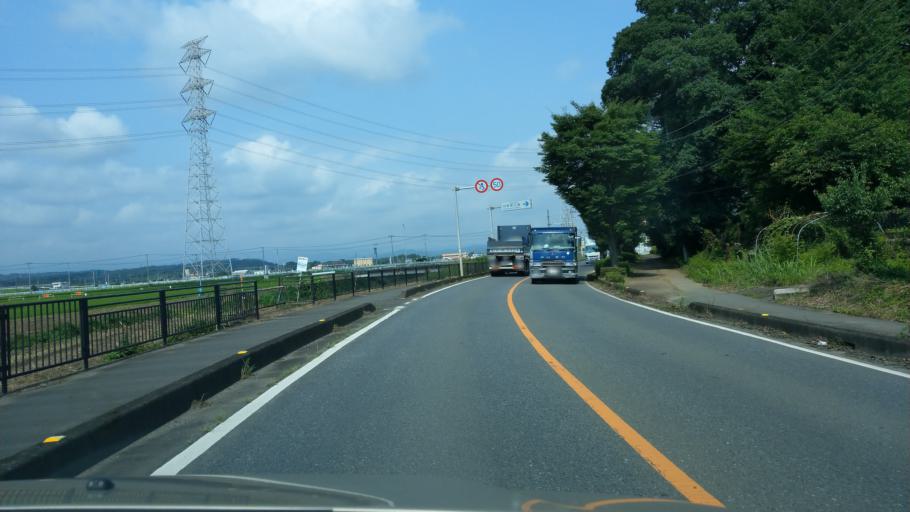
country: JP
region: Saitama
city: Sakado
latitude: 36.0167
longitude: 139.4130
